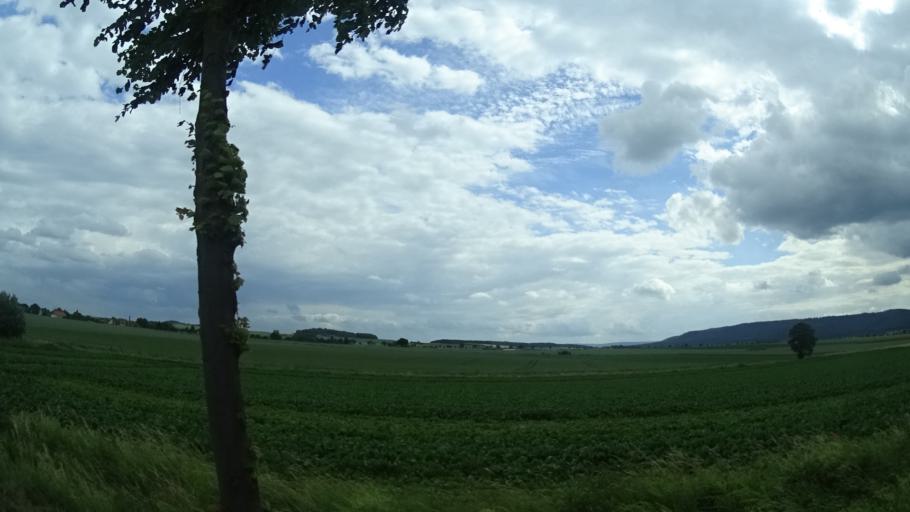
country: DE
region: Lower Saxony
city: Elze
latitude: 52.1700
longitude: 9.6987
